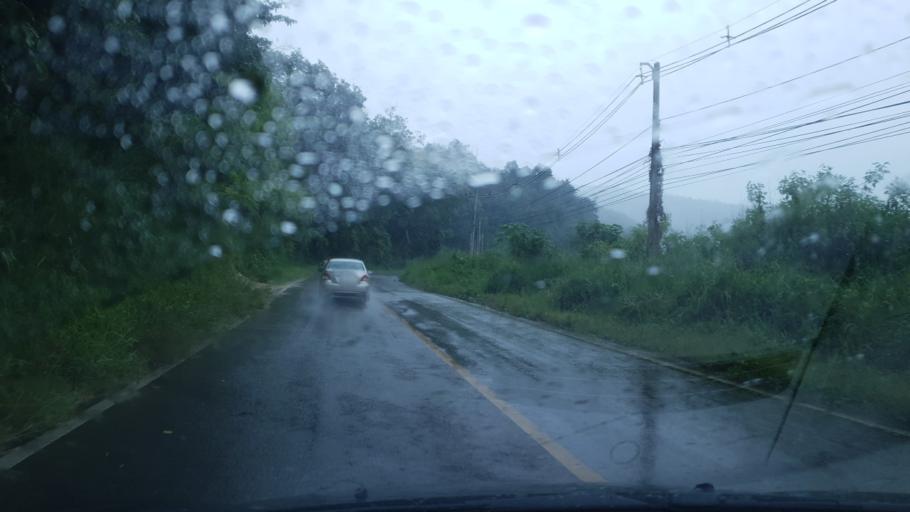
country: TH
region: Mae Hong Son
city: Khun Yuam
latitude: 18.6605
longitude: 97.9302
